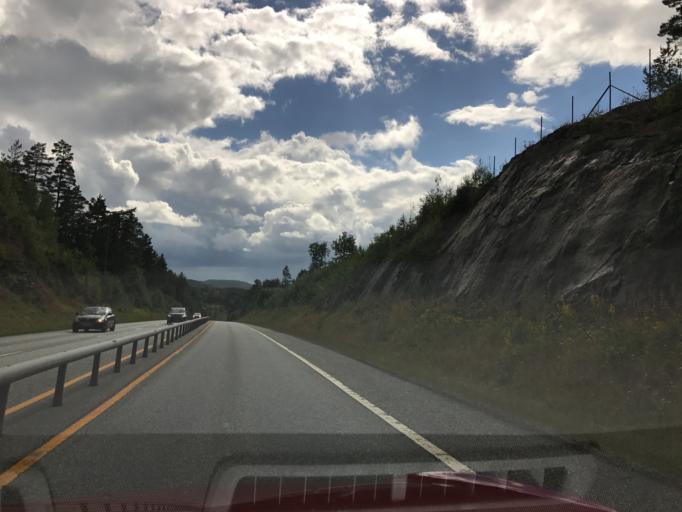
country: NO
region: Aust-Agder
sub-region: Gjerstad
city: Gjerstad
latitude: 58.8500
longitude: 9.1176
